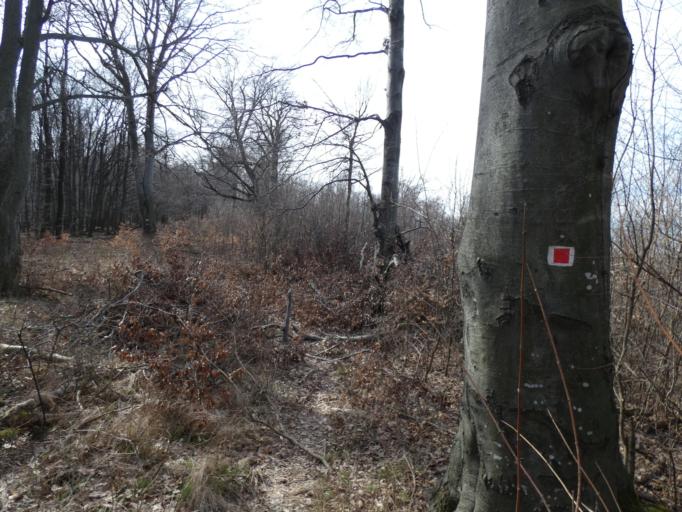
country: HU
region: Nograd
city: Diosjeno
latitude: 47.9718
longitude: 18.9544
